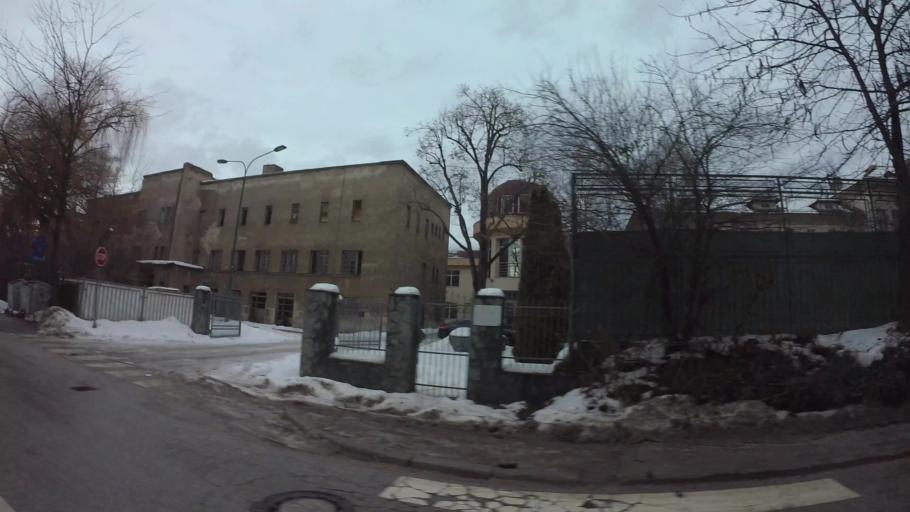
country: BA
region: Federation of Bosnia and Herzegovina
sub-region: Kanton Sarajevo
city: Sarajevo
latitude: 43.8541
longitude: 18.3712
